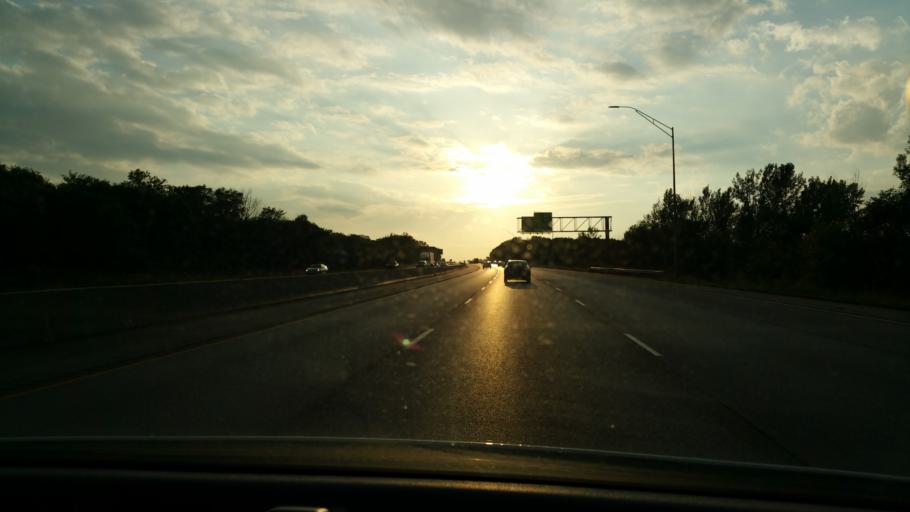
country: US
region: Iowa
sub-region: Polk County
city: Johnston
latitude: 41.6529
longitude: -93.7119
